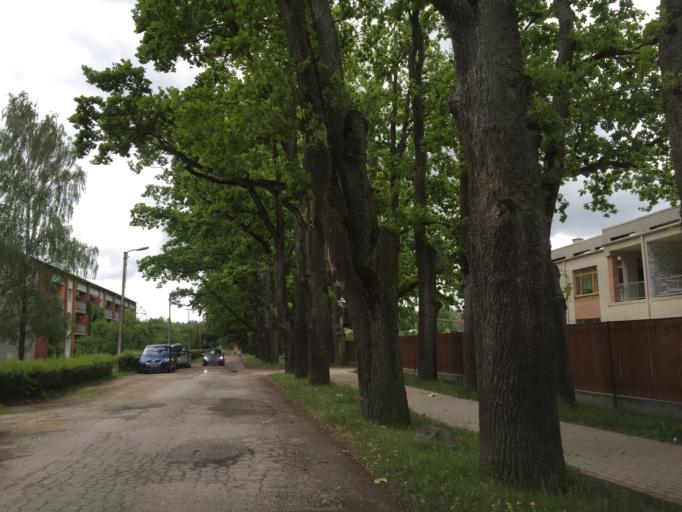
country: LV
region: Lecava
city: Iecava
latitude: 56.5917
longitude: 24.2024
